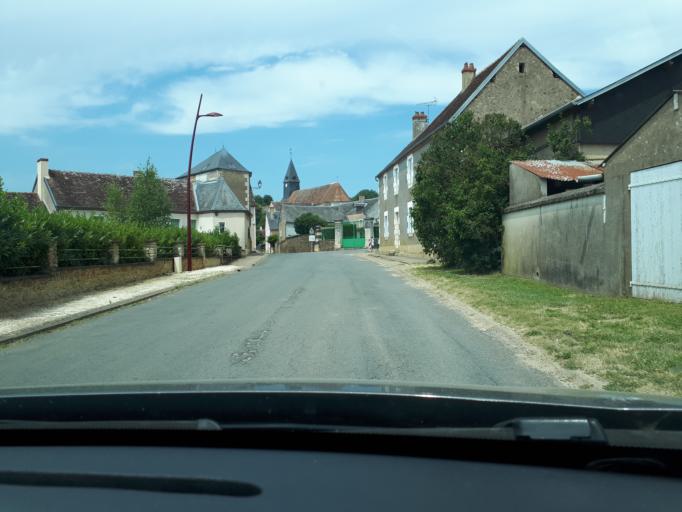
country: FR
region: Centre
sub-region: Departement du Cher
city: Sancerre
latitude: 47.3046
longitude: 2.7453
